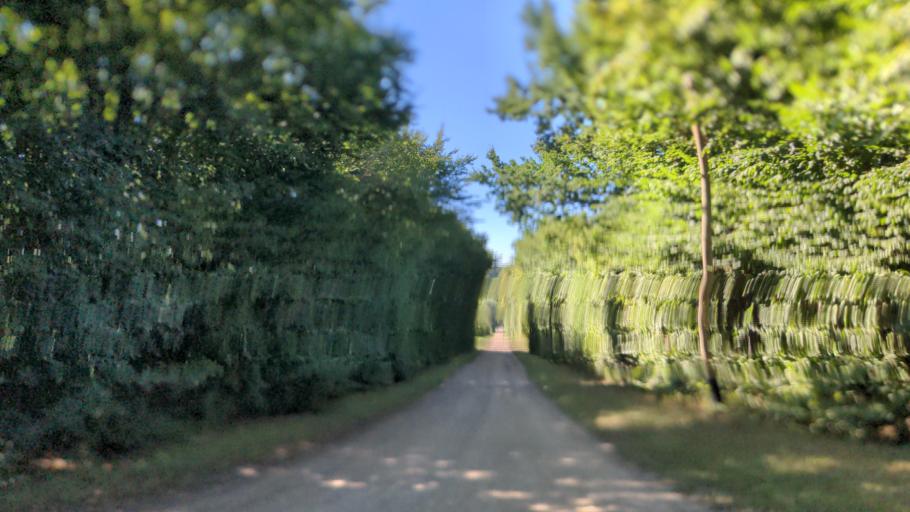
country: DE
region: Mecklenburg-Vorpommern
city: Selmsdorf
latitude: 53.8384
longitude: 10.8538
